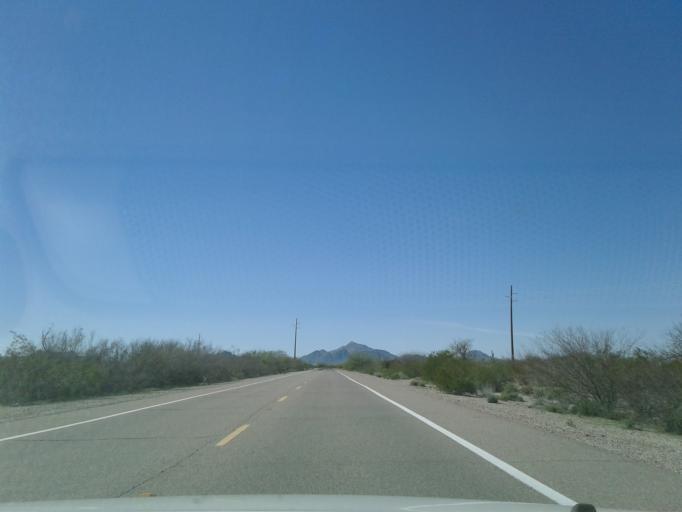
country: US
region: Arizona
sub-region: Pima County
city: Avra Valley
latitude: 32.3773
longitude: -111.3556
